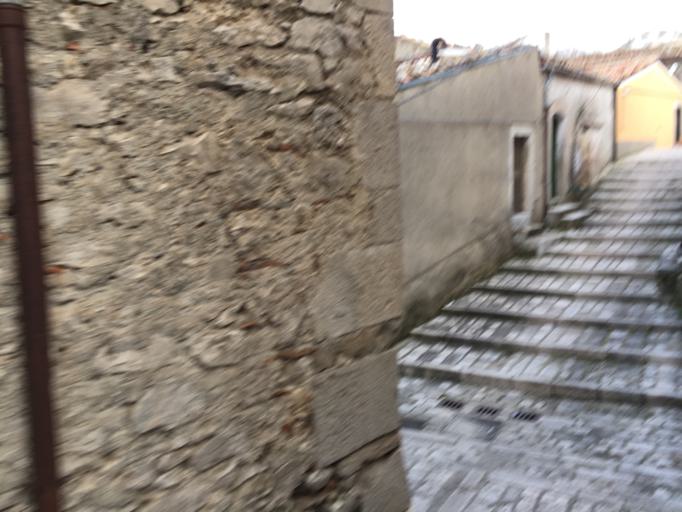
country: IT
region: Molise
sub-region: Provincia di Campobasso
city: Guardiaregia
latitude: 41.4348
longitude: 14.5413
